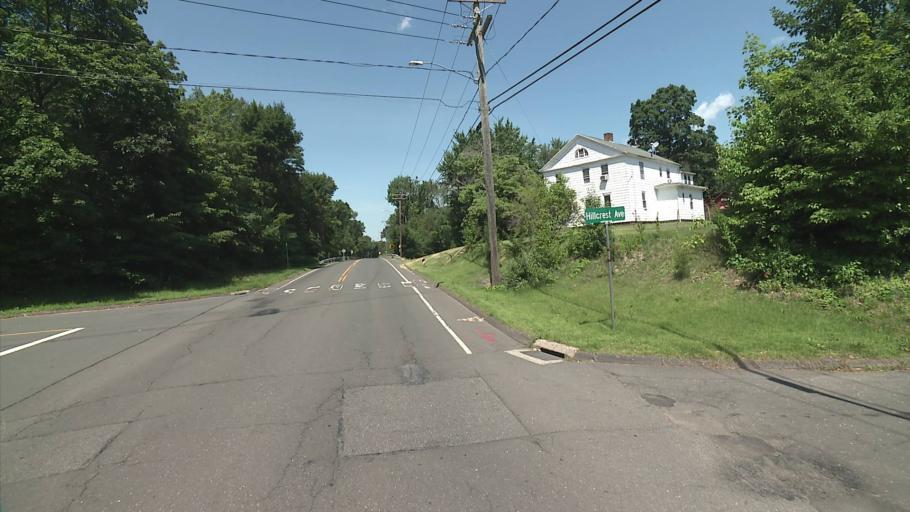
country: US
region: Connecticut
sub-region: Hartford County
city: Kensington
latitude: 41.6367
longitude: -72.7718
